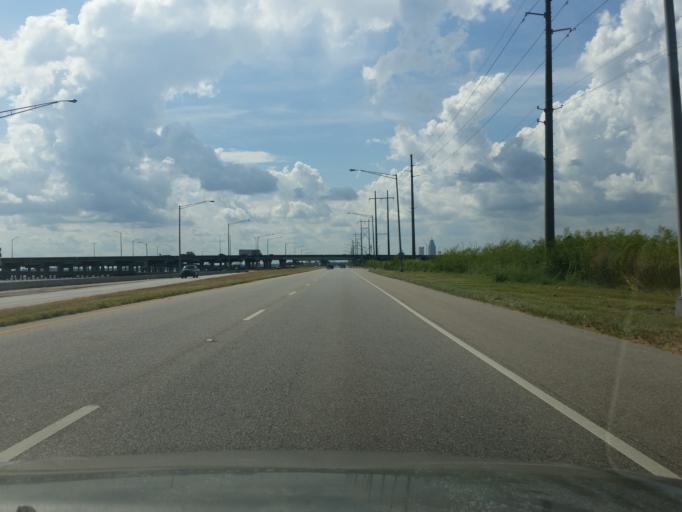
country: US
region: Alabama
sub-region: Mobile County
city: Mobile
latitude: 30.6773
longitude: -87.9814
